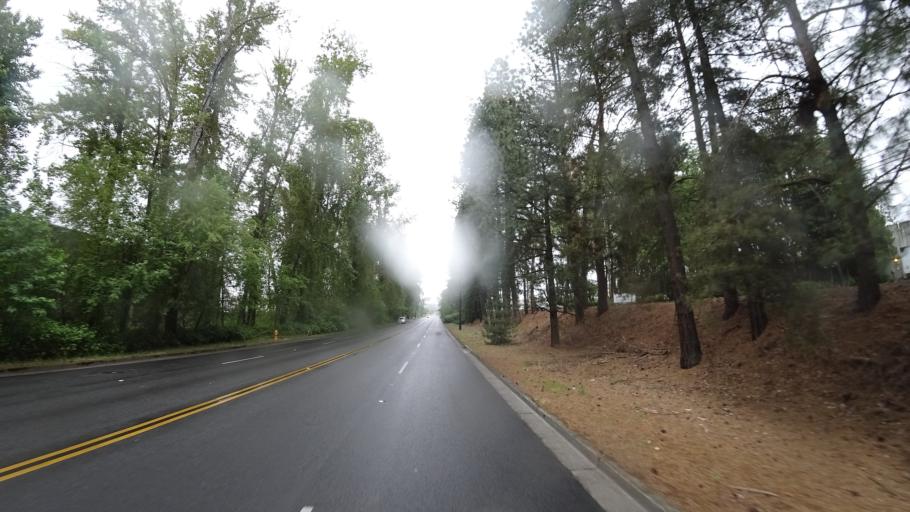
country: US
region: Oregon
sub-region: Washington County
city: Raleigh Hills
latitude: 45.4774
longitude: -122.7828
